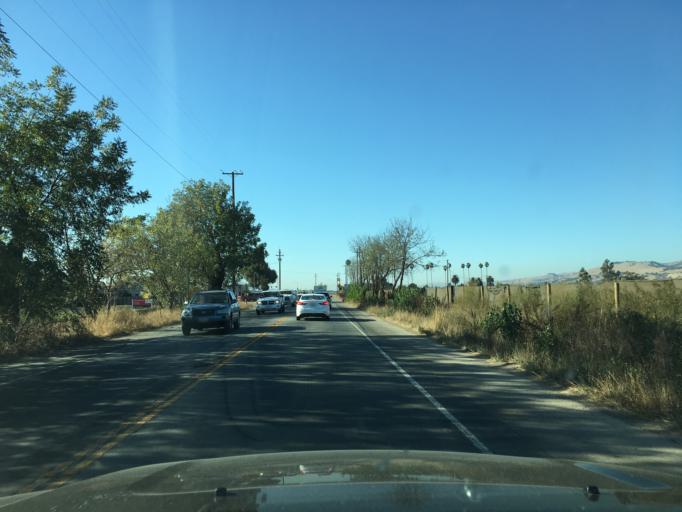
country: US
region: California
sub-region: Santa Clara County
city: Gilroy
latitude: 37.0074
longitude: -121.5125
